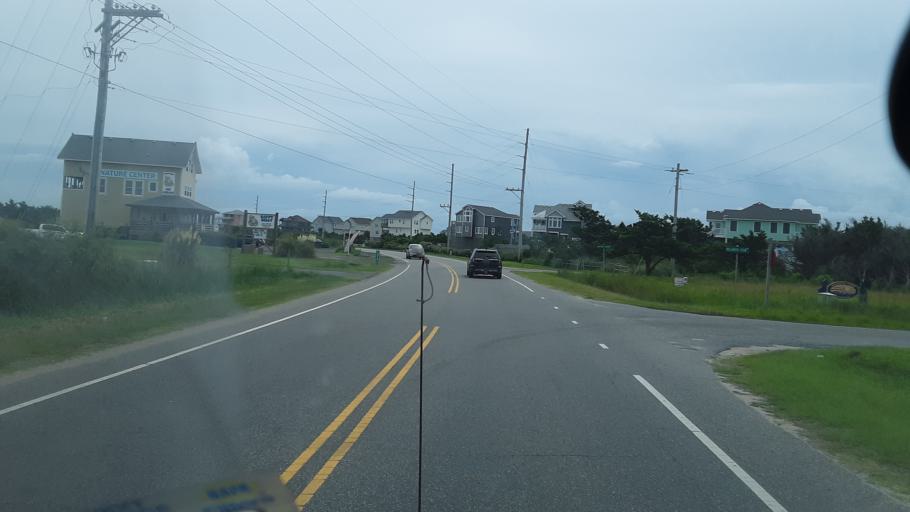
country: US
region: North Carolina
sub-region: Dare County
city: Buxton
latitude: 35.2152
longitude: -75.6844
